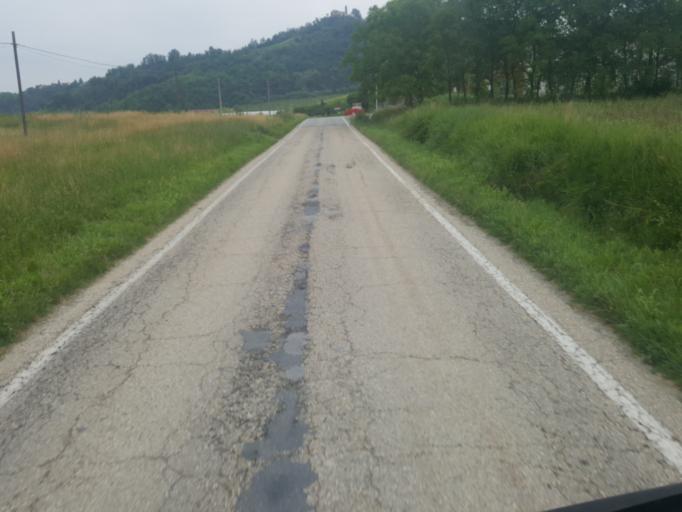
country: IT
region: Piedmont
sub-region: Provincia di Cuneo
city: Vezza d'Alba
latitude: 44.7637
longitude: 8.0177
